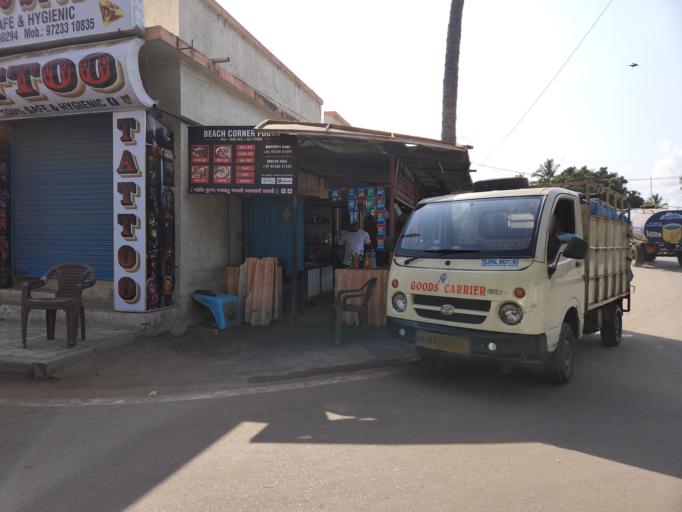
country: IN
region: Daman and Diu
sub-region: Daman District
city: Daman
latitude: 20.3769
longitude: 72.8243
